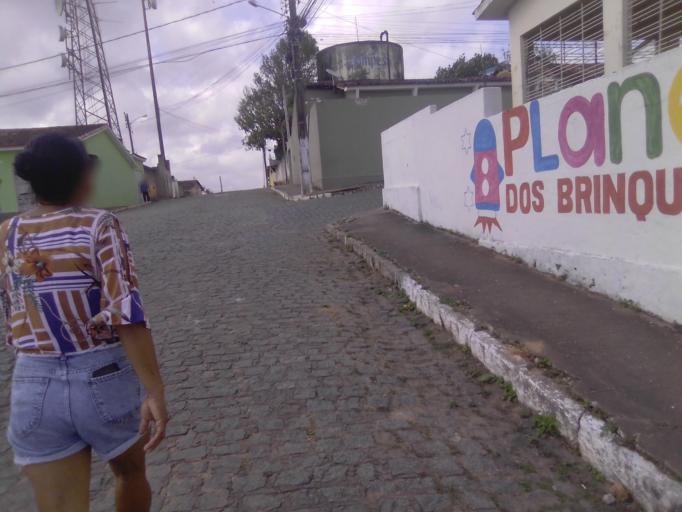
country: BR
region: Pernambuco
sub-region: Vicencia
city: Vicencia
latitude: -7.6614
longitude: -35.3226
